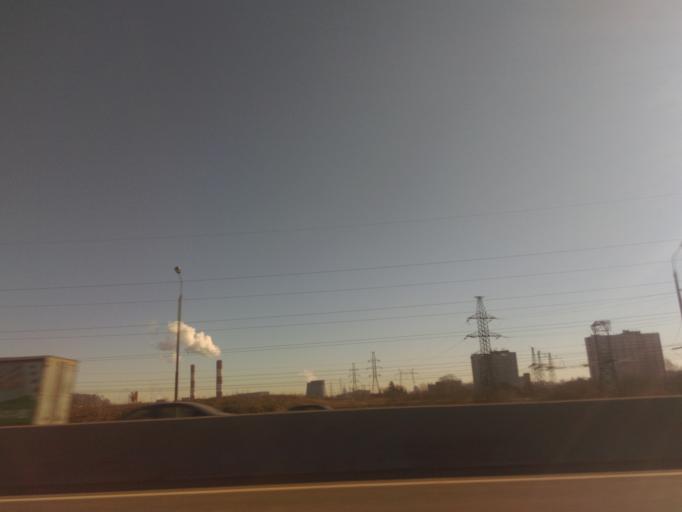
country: RU
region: Moscow
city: Mikhalkovo
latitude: 55.6871
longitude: 37.4148
